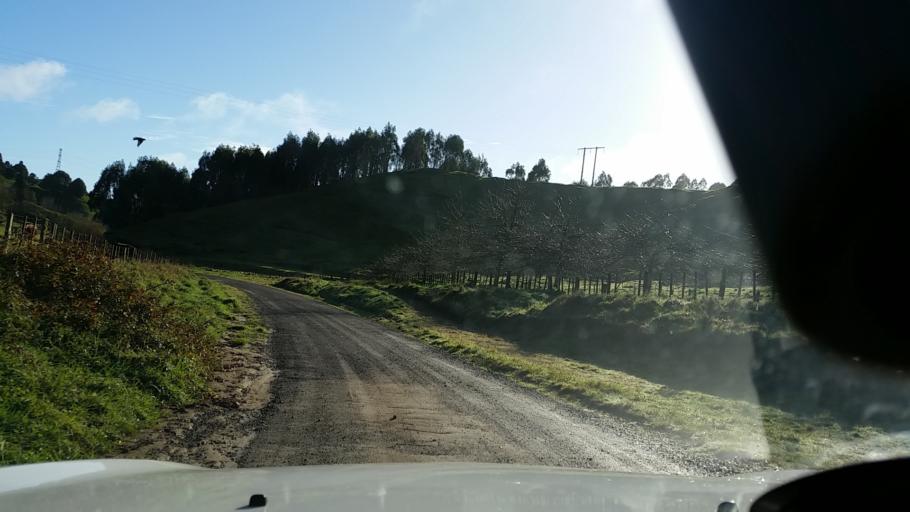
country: NZ
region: Bay of Plenty
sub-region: Kawerau District
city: Kawerau
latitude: -38.0171
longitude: 176.5978
